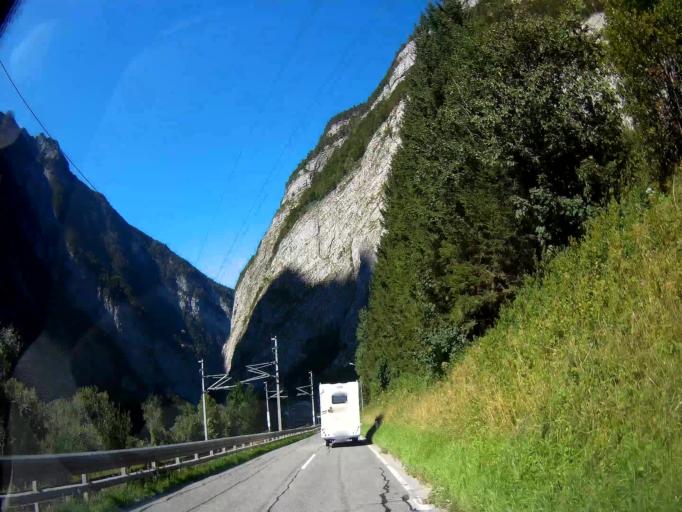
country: AT
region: Salzburg
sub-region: Politischer Bezirk Hallein
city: Golling an der Salzach
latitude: 47.5497
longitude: 13.1705
